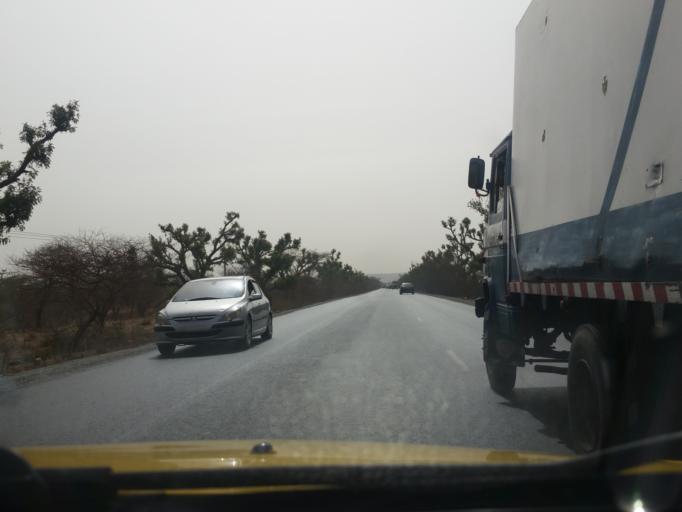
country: SN
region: Thies
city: Pout
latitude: 14.7632
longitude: -17.0235
